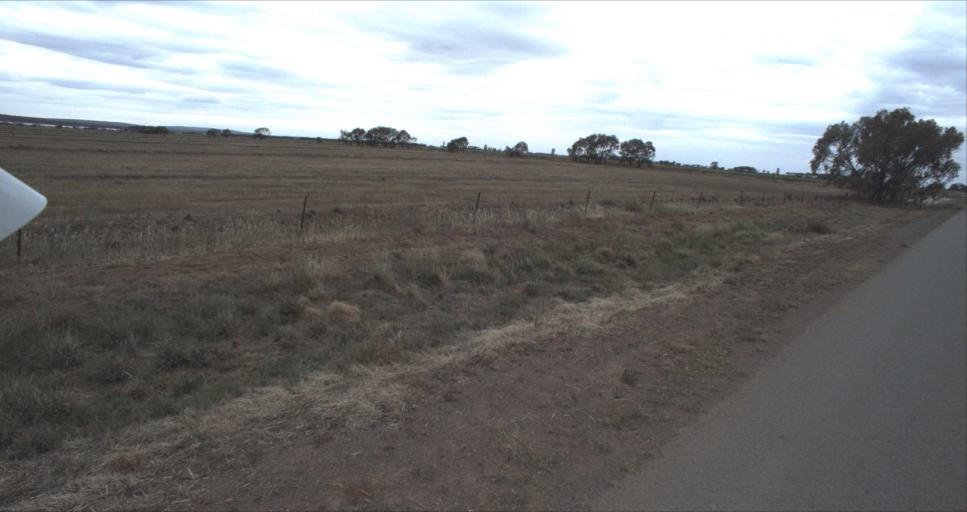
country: AU
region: New South Wales
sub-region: Leeton
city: Leeton
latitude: -34.4214
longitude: 146.3384
